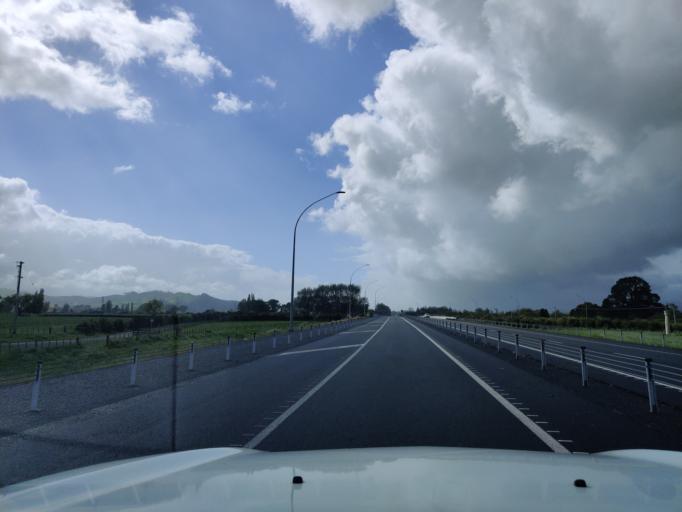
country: NZ
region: Waikato
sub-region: Waipa District
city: Cambridge
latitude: -37.8937
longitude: 175.5027
